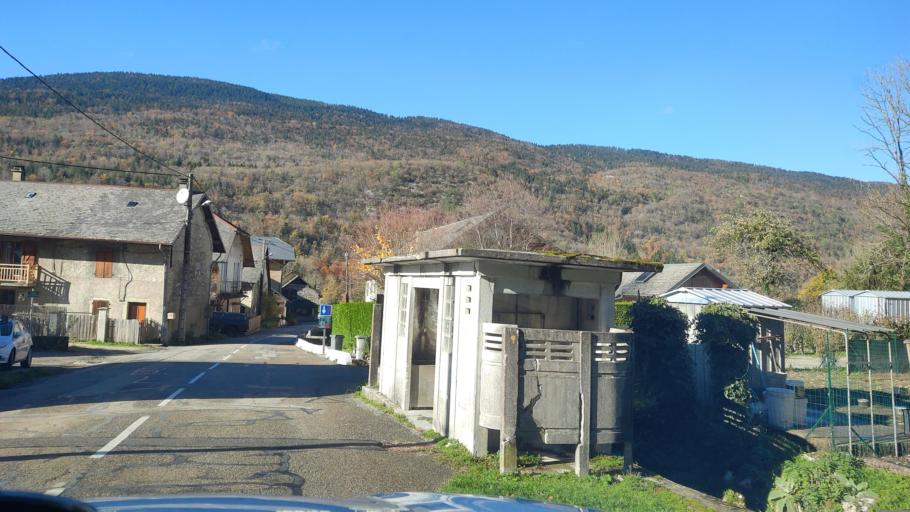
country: FR
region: Rhone-Alpes
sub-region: Departement de la Savoie
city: Les Echelles
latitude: 45.4661
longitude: 5.8210
